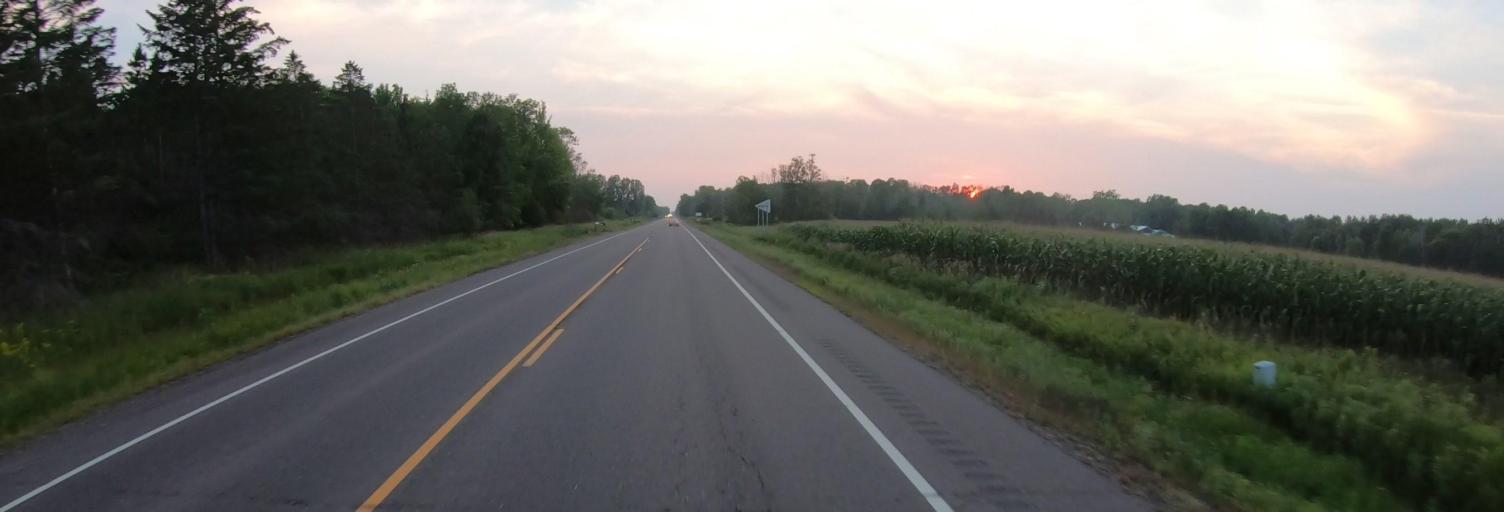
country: US
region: Minnesota
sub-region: Pine County
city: Rock Creek
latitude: 45.7734
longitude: -92.8619
